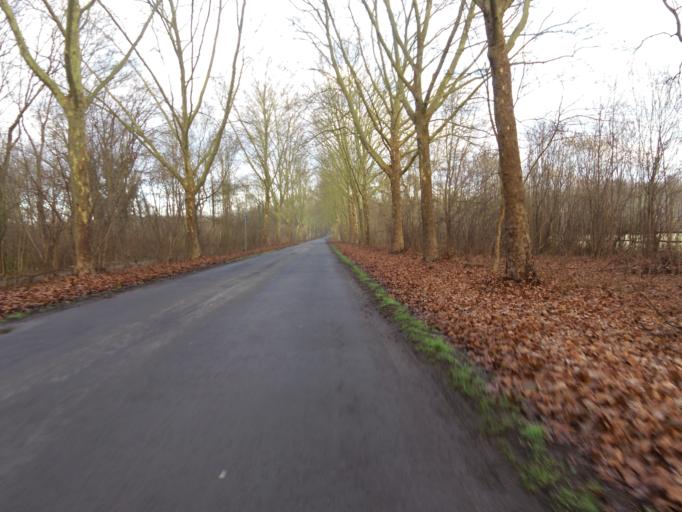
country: DE
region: Rheinland-Pfalz
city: Worms
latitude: 49.6169
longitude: 8.3803
